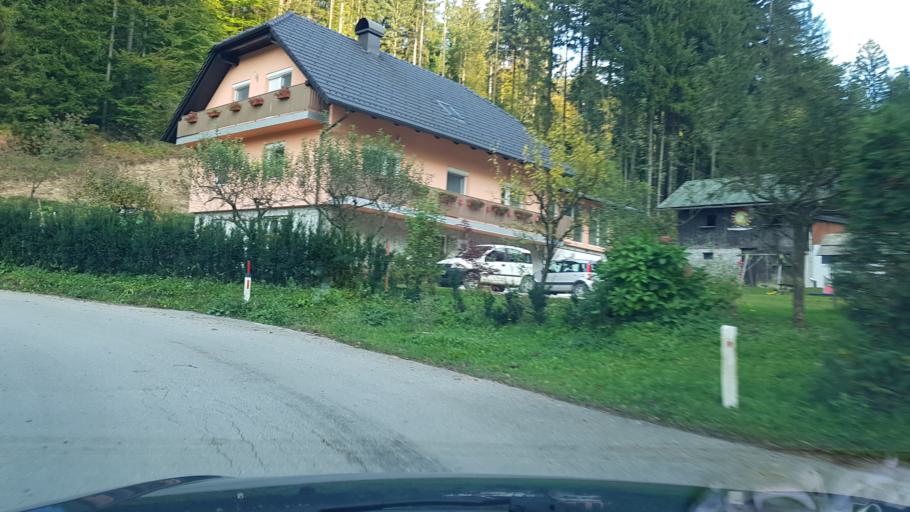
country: SI
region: Slovenj Gradec
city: Smartno pri Slovenj Gradcu
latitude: 46.5094
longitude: 15.1107
